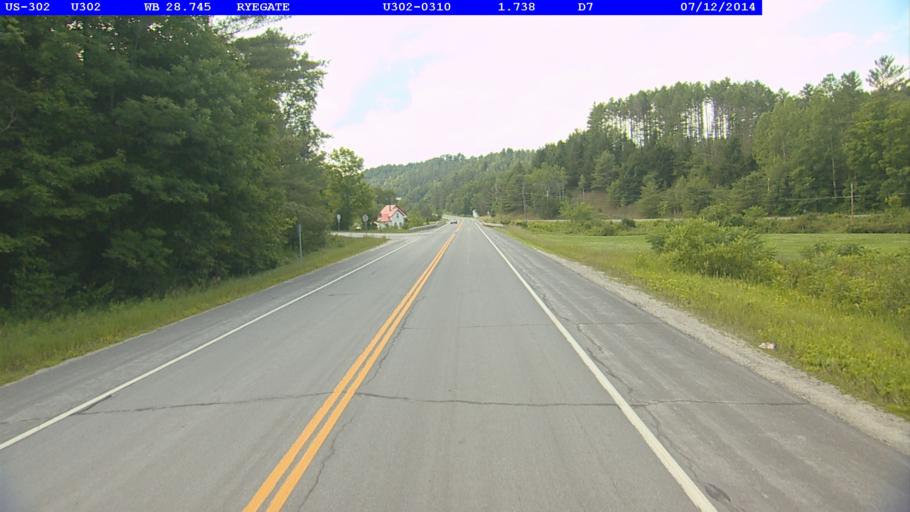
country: US
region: New Hampshire
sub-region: Grafton County
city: Woodsville
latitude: 44.1899
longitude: -72.1457
